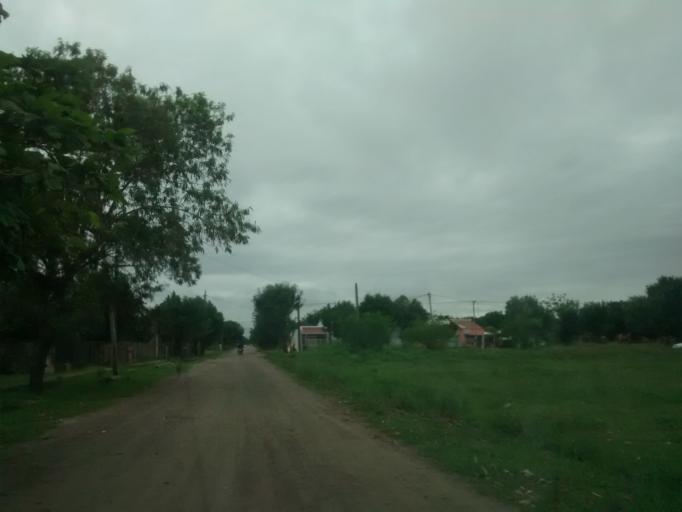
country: AR
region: Chaco
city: Puerto Tirol
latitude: -27.3741
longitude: -59.1005
